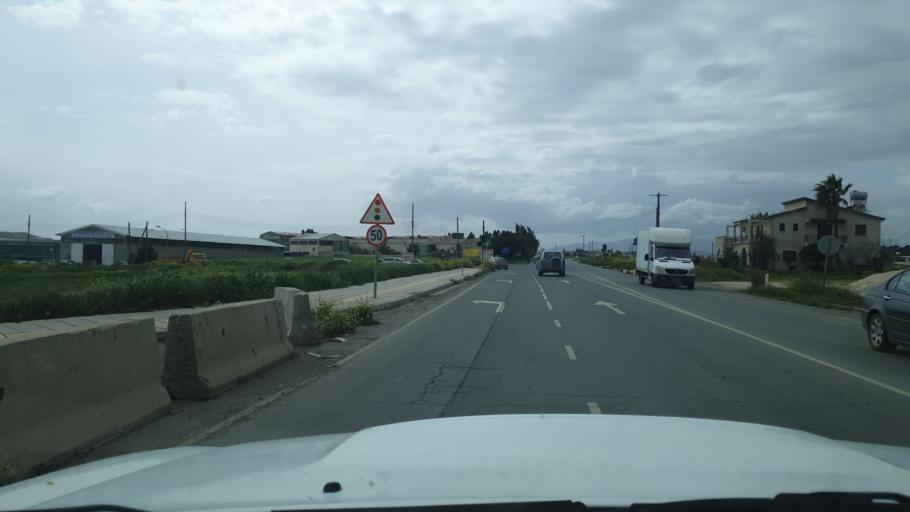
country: CY
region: Lefkosia
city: Tseri
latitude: 35.1058
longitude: 33.3302
